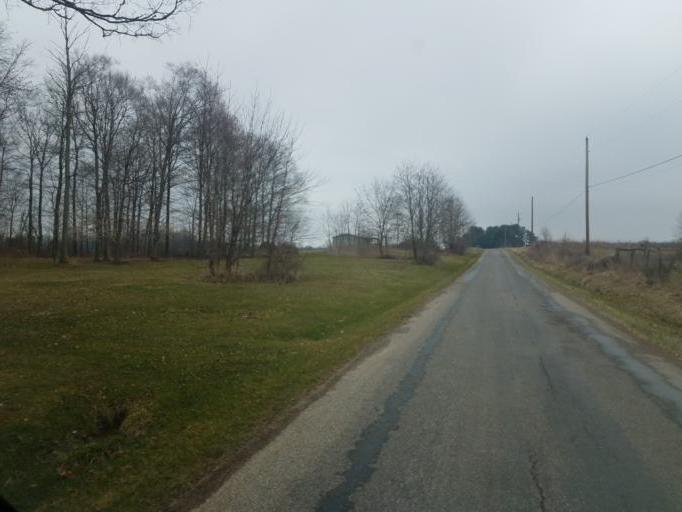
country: US
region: Ohio
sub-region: Sandusky County
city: Bellville
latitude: 40.5774
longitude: -82.6020
